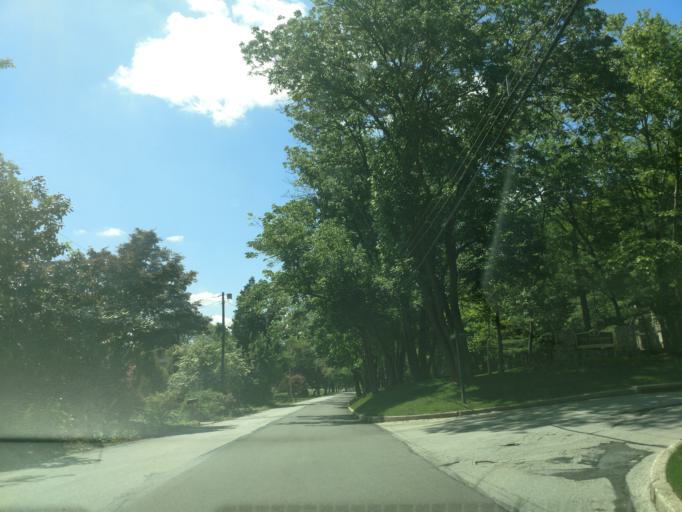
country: US
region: Pennsylvania
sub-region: Montgomery County
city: King of Prussia
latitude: 40.1026
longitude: -75.4162
